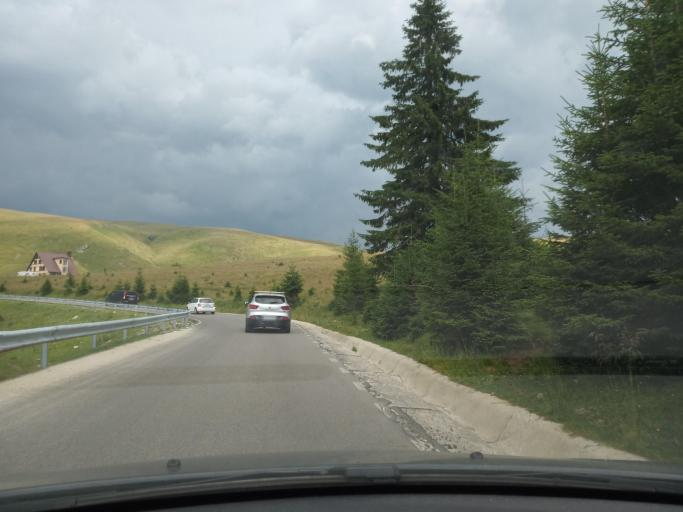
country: RO
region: Dambovita
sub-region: Comuna Moroeni
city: Glod
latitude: 45.3252
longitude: 25.4612
